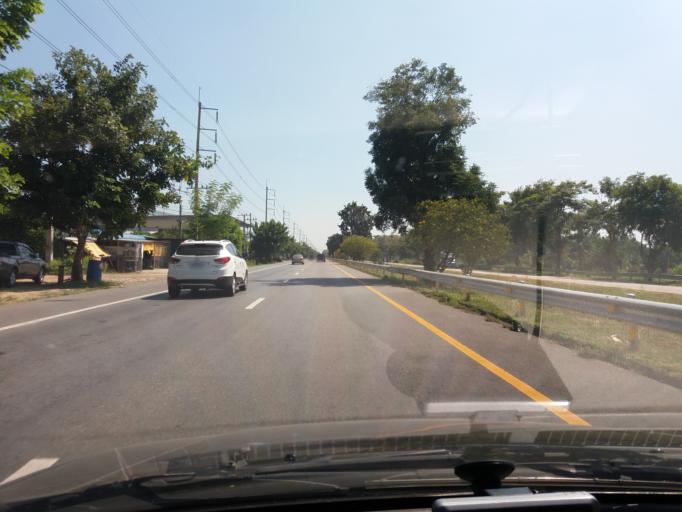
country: TH
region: Chai Nat
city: Chai Nat
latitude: 15.1335
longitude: 100.1452
